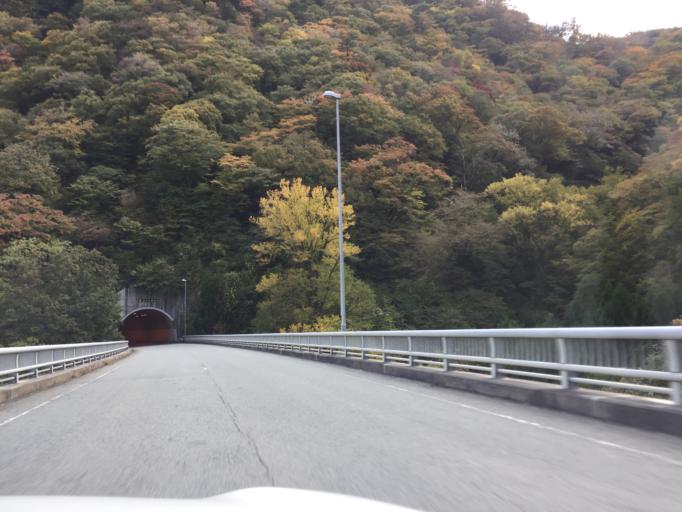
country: JP
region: Fukushima
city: Namie
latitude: 37.3562
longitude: 140.9386
